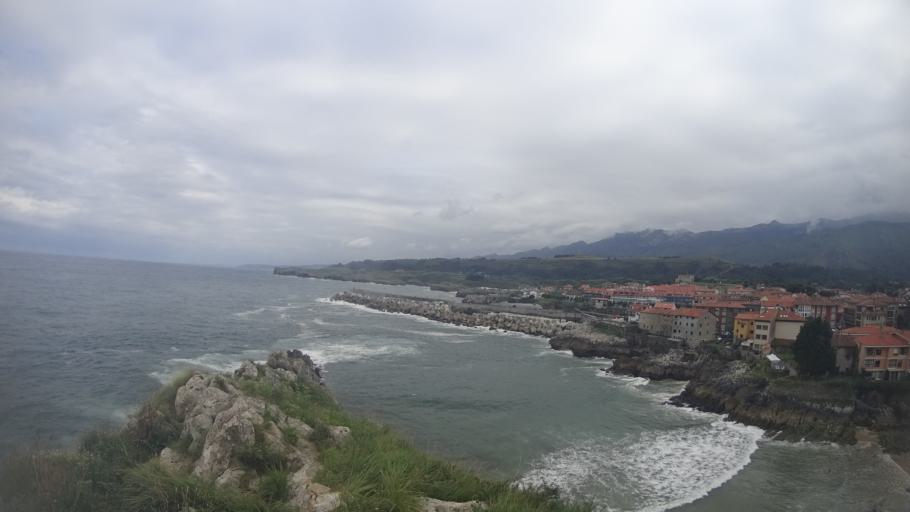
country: ES
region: Asturias
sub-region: Province of Asturias
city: Llanes
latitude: 43.4234
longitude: -4.7521
